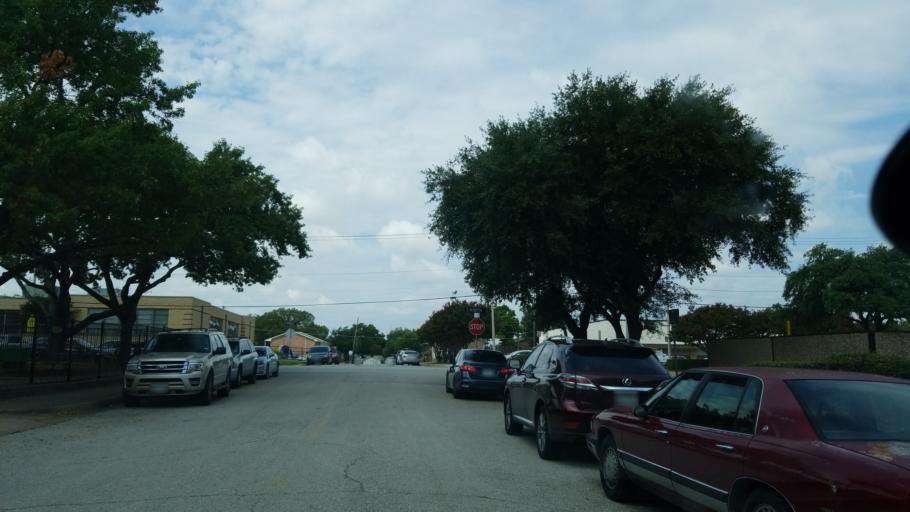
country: US
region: Texas
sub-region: Dallas County
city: Garland
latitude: 32.9118
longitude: -96.6409
